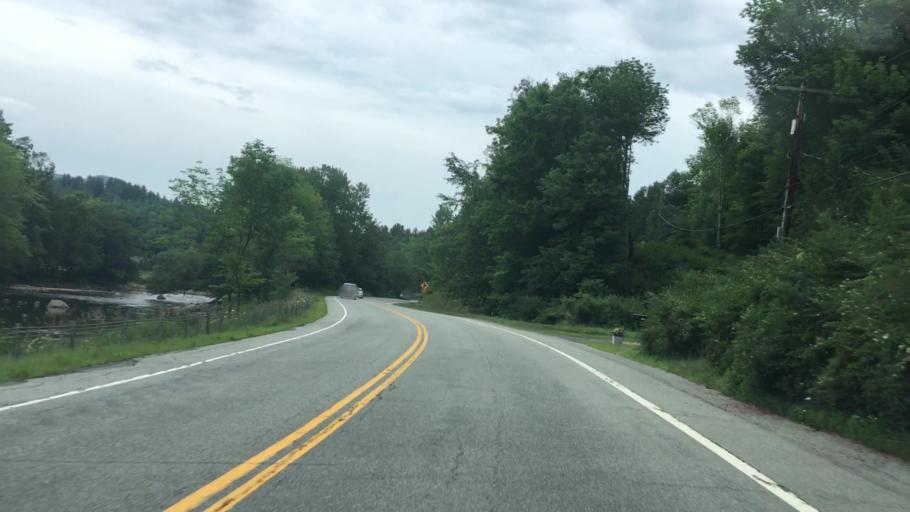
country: US
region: New York
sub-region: Essex County
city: Lake Placid
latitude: 44.2767
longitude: -73.7898
